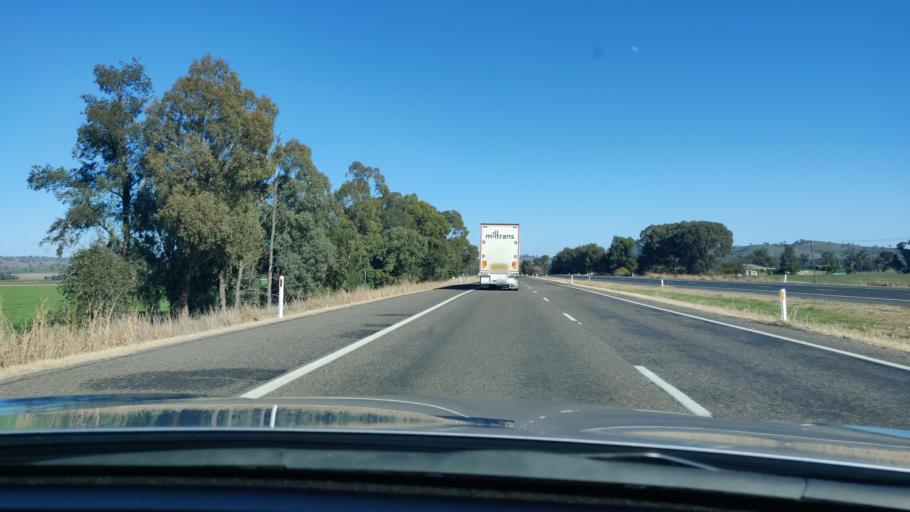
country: AU
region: New South Wales
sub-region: Gundagai
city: Gundagai
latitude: -35.1072
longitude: 148.0602
